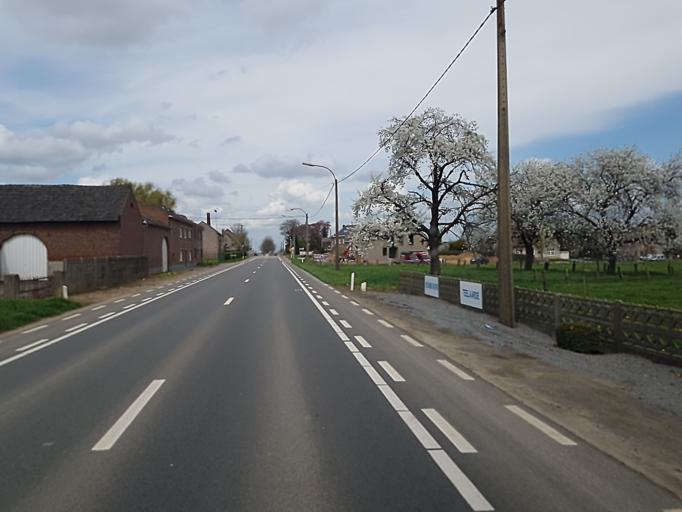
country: BE
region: Flanders
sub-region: Provincie Limburg
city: Riemst
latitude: 50.8348
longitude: 5.6256
